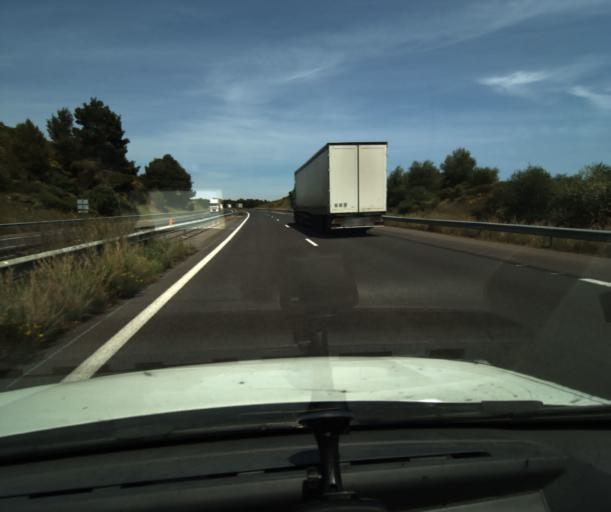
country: FR
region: Languedoc-Roussillon
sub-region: Departement des Pyrenees-Orientales
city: Banyuls-dels-Aspres
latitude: 42.5464
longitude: 2.8489
